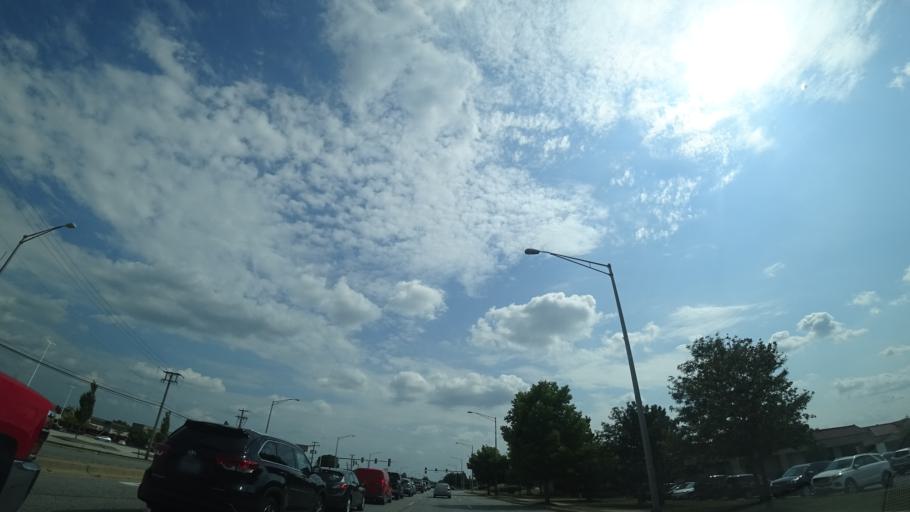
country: US
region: Illinois
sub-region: Cook County
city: Tinley Park
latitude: 41.5997
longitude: -87.7942
